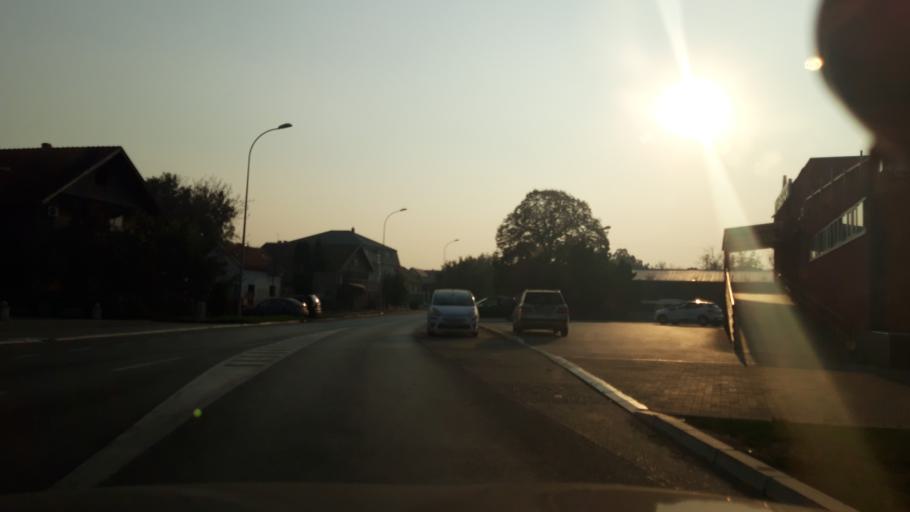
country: RS
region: Autonomna Pokrajina Vojvodina
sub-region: Sremski Okrug
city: Ingija
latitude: 45.0408
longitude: 20.0876
